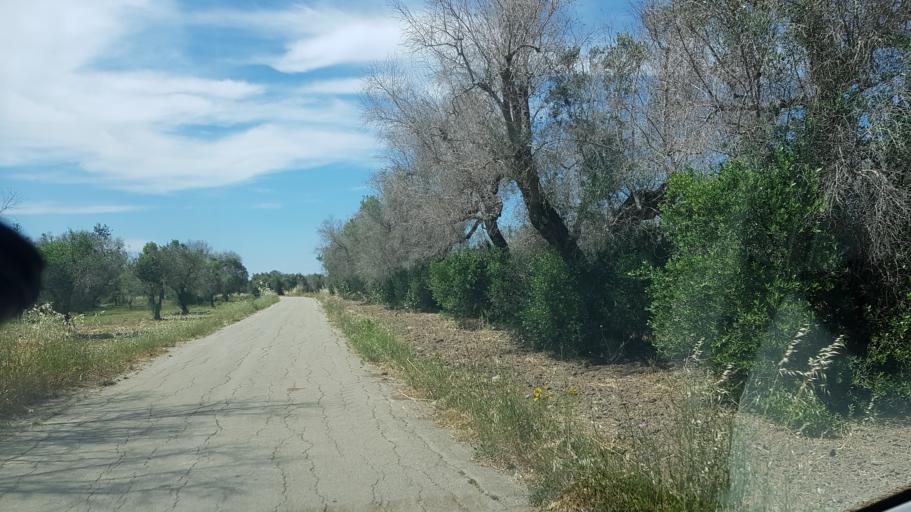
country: IT
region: Apulia
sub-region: Provincia di Brindisi
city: San Pietro Vernotico
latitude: 40.5267
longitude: 18.0067
